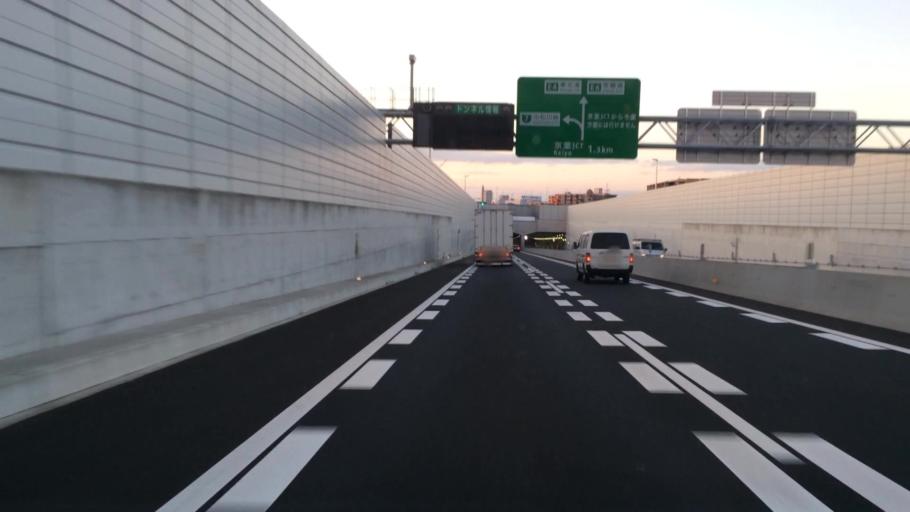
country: JP
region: Chiba
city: Funabashi
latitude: 35.6958
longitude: 139.9382
